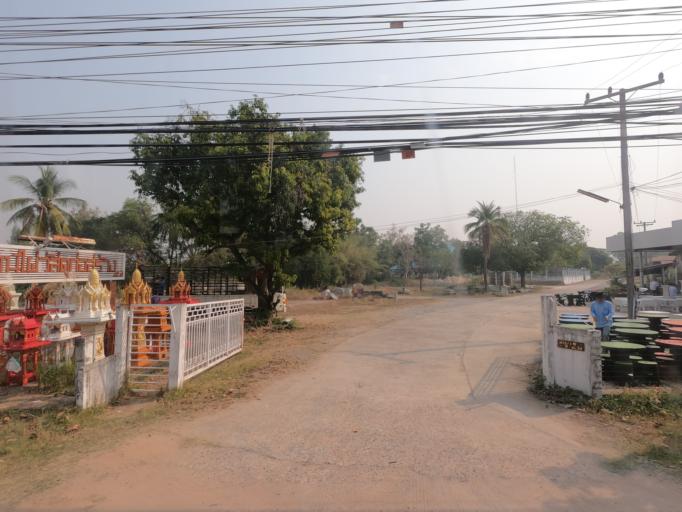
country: TH
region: Khon Kaen
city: Ban Phai
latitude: 16.0650
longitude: 102.7230
